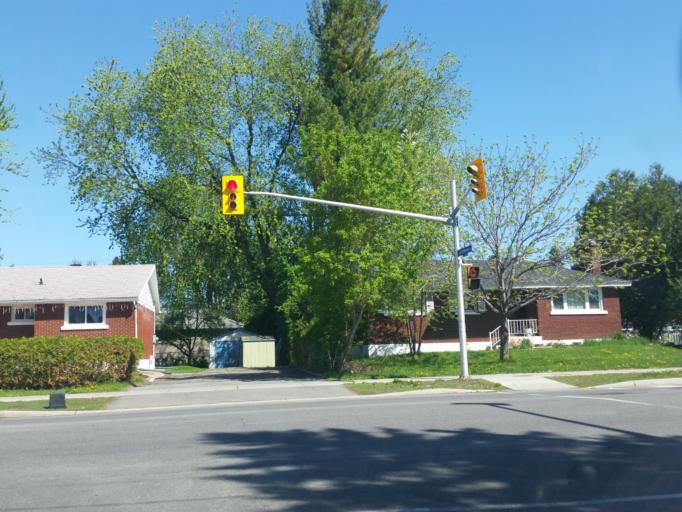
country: CA
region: Ontario
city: Ottawa
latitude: 45.3453
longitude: -75.7478
